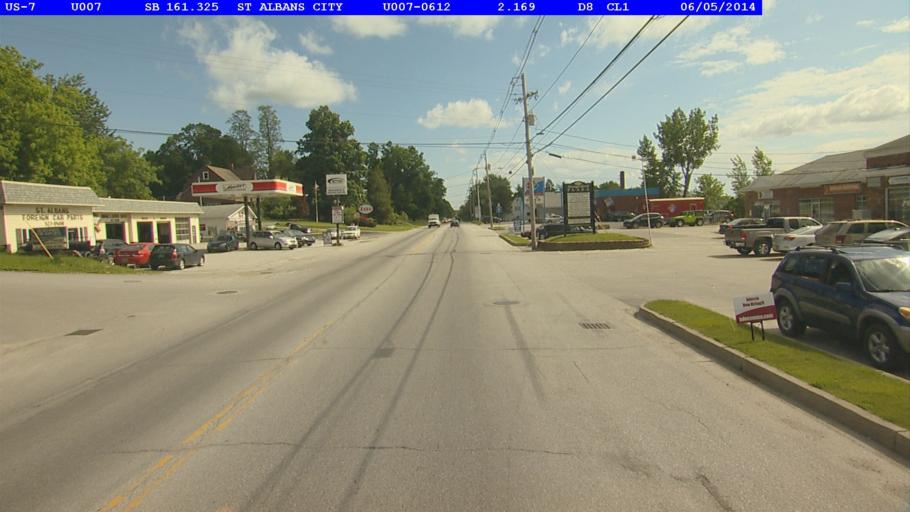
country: US
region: Vermont
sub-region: Franklin County
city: Saint Albans
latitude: 44.8239
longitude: -73.0810
